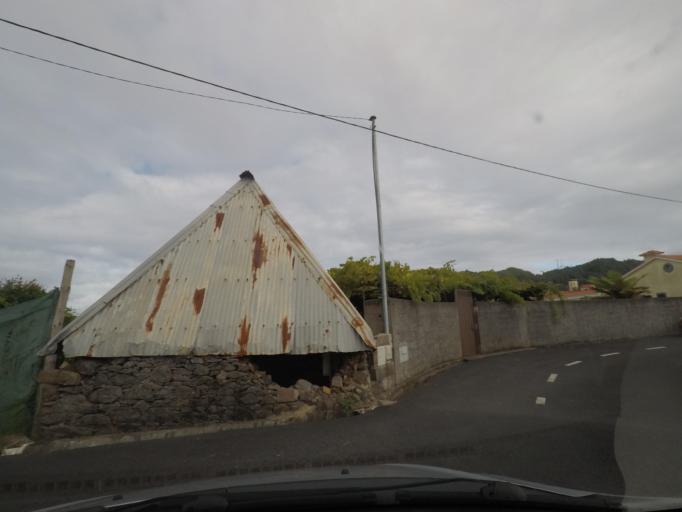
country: PT
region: Madeira
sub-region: Santana
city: Santana
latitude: 32.8109
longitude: -16.8767
